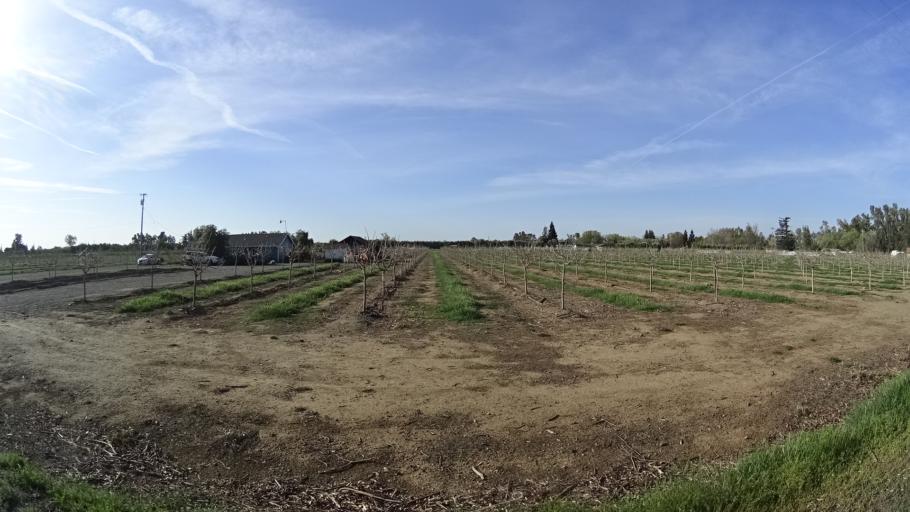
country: US
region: California
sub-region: Glenn County
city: Orland
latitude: 39.7154
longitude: -122.2139
